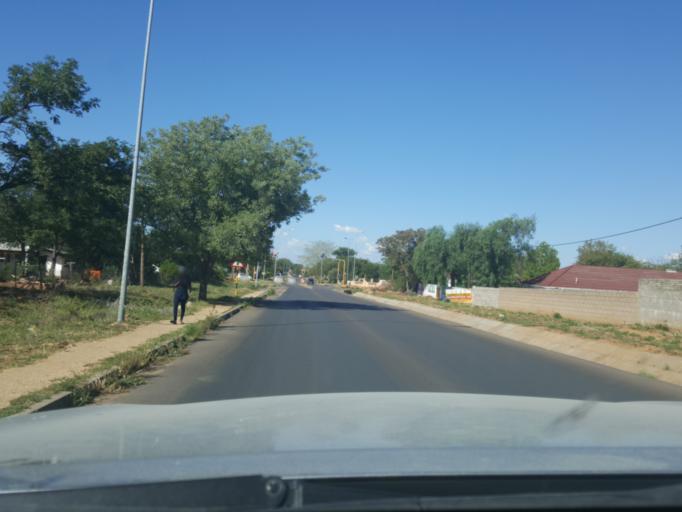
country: BW
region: South East
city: Gaborone
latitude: -24.6263
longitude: 25.9417
